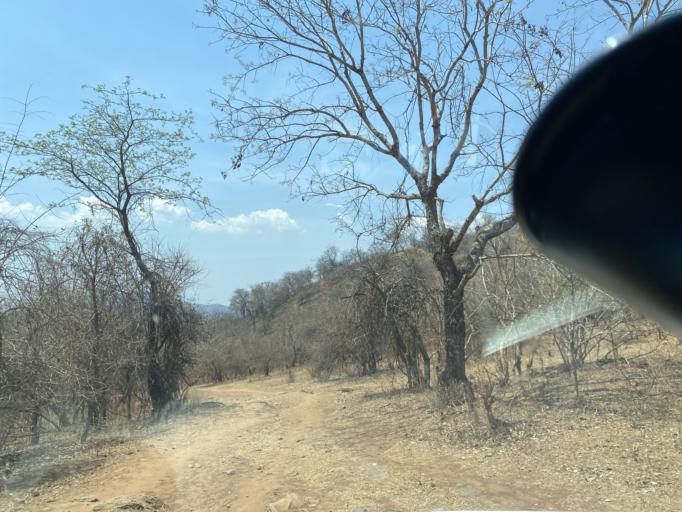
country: ZM
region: Lusaka
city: Kafue
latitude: -15.7933
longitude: 28.4562
